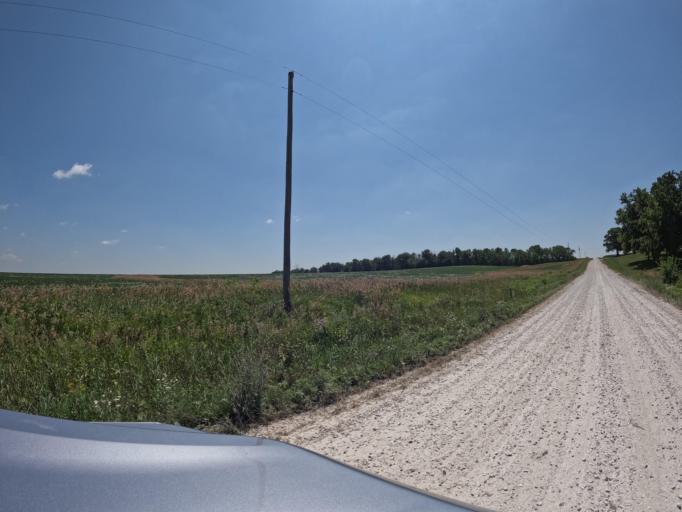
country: US
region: Iowa
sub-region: Keokuk County
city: Sigourney
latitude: 41.2851
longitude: -92.2382
